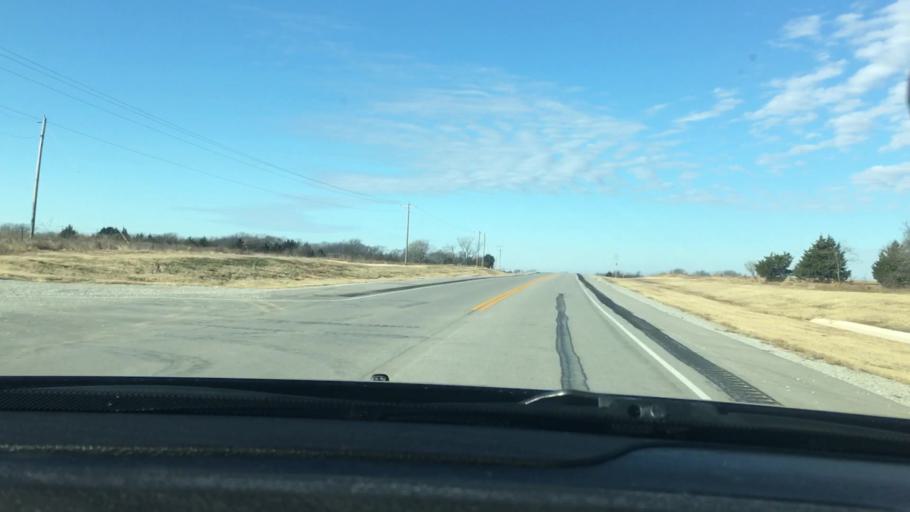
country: US
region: Oklahoma
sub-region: Love County
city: Marietta
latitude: 33.9403
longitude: -97.2474
